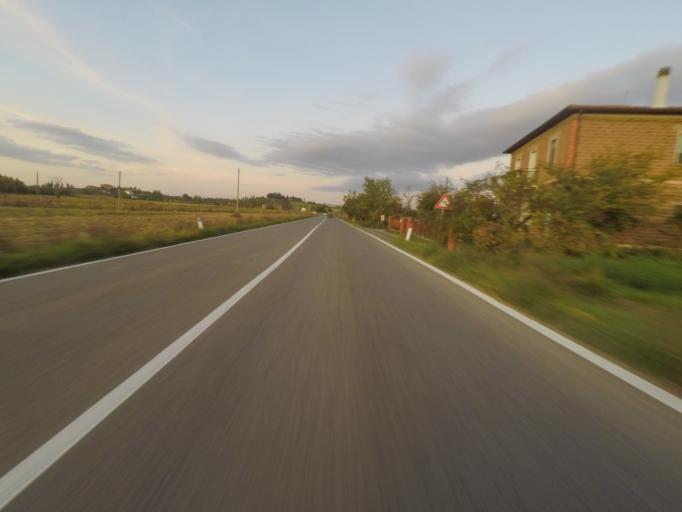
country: IT
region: Tuscany
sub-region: Provincia di Siena
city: Guazzino
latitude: 43.2010
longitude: 11.7636
